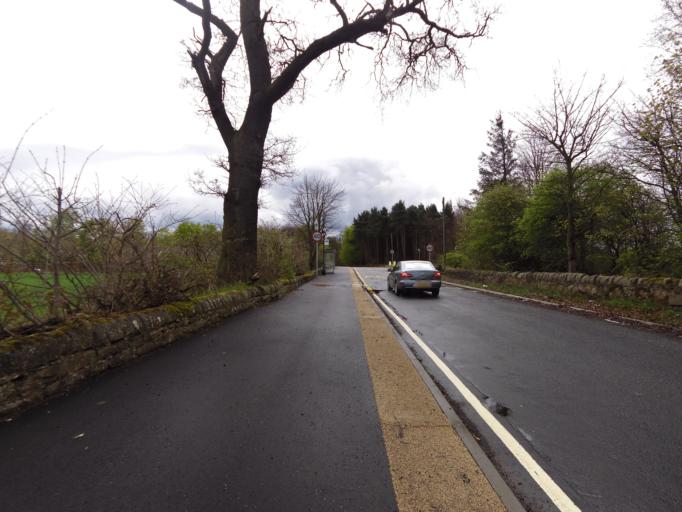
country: GB
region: Scotland
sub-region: Edinburgh
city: Ratho
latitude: 55.9719
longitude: -3.3285
